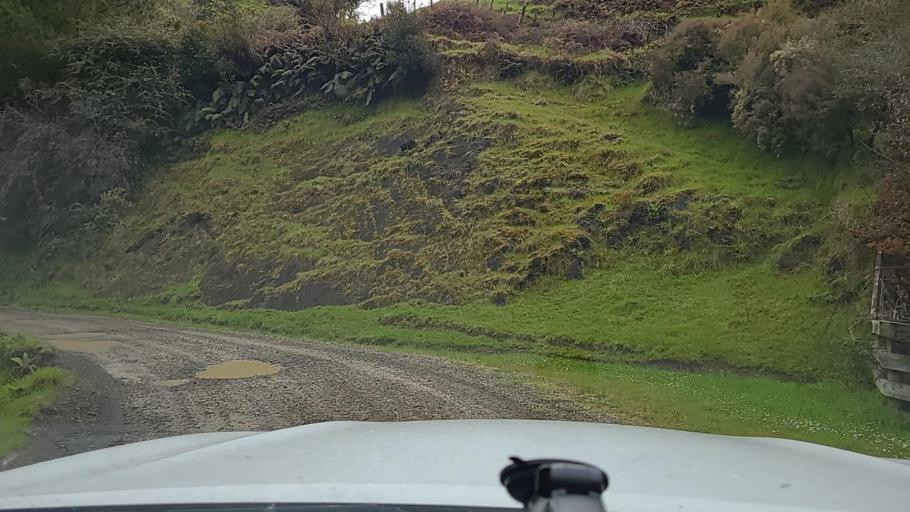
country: NZ
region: Bay of Plenty
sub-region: Opotiki District
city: Opotiki
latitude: -38.2417
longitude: 177.6103
